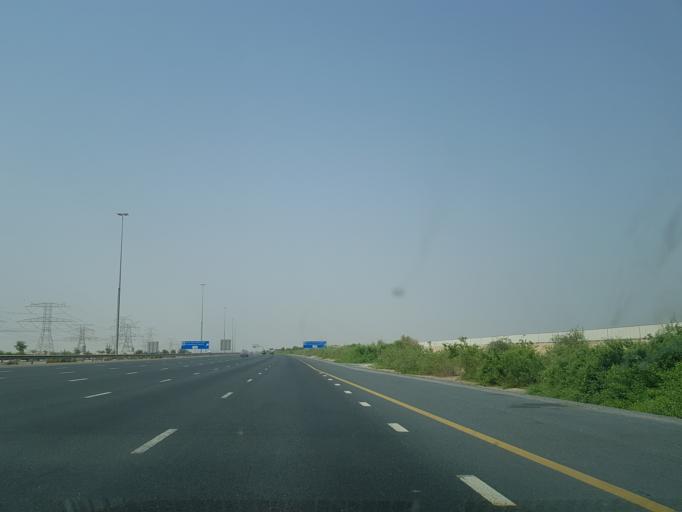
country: AE
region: Dubai
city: Dubai
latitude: 25.0569
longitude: 55.3172
